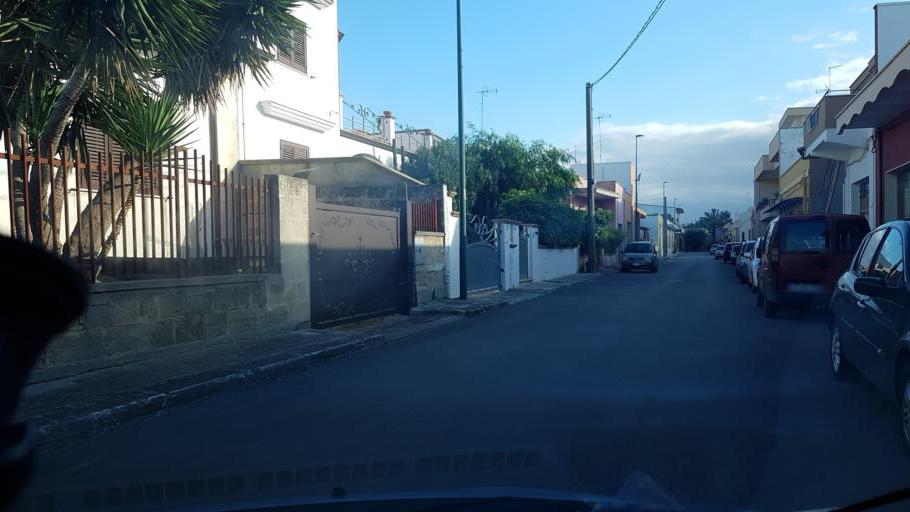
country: IT
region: Apulia
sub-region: Provincia di Lecce
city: Guagnano
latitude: 40.4038
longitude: 17.9546
